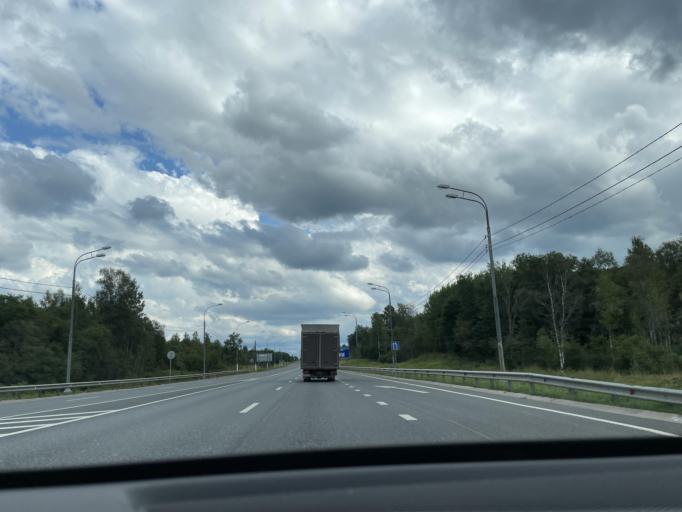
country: RU
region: Novgorod
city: Valday
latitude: 57.9929
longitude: 33.1877
